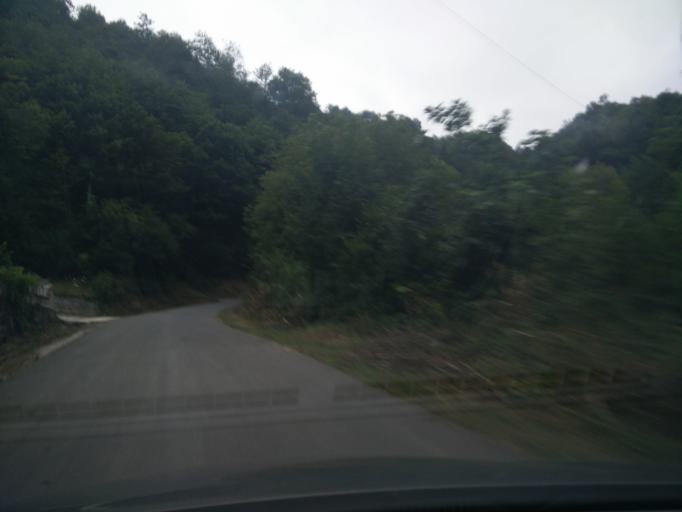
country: ES
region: Asturias
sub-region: Province of Asturias
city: Campo de Caso
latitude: 43.1529
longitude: -5.3890
